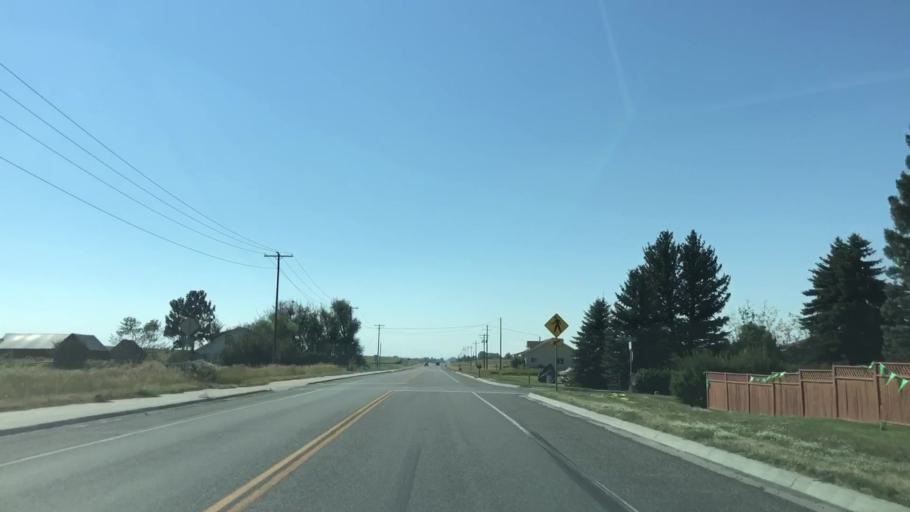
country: US
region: Montana
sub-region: Gallatin County
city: Bozeman
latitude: 45.7292
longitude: -111.1003
